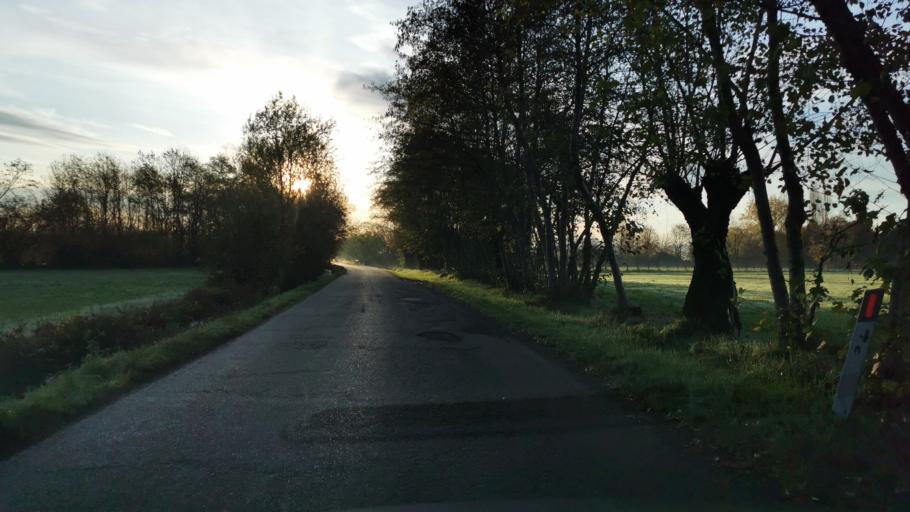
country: IT
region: Piedmont
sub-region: Provincia di Torino
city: San Francesco al Campo
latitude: 45.2071
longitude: 7.6620
